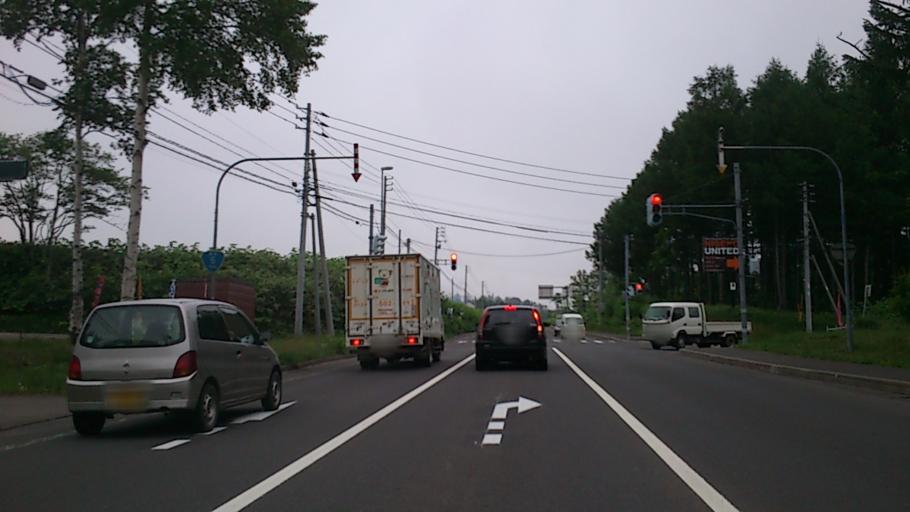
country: JP
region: Hokkaido
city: Niseko Town
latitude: 42.8636
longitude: 140.7455
